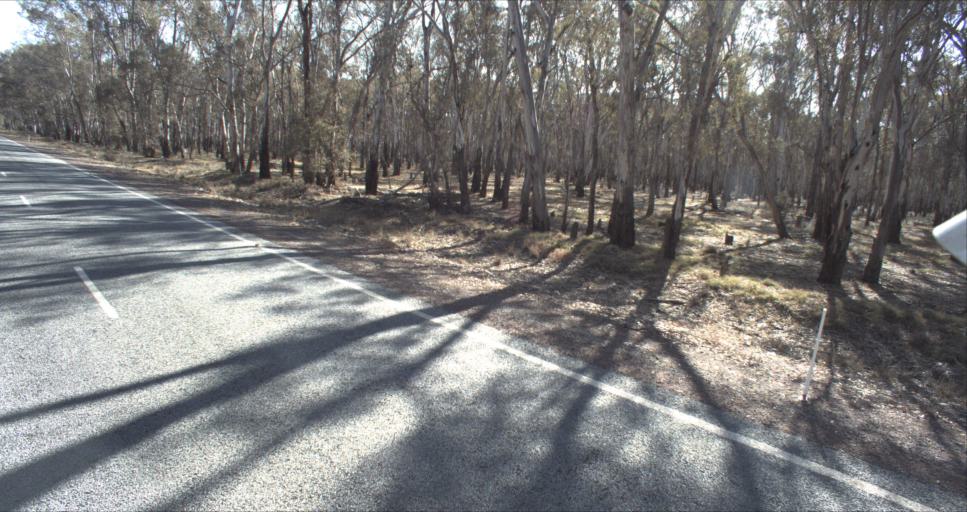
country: AU
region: New South Wales
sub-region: Leeton
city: Leeton
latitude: -34.6271
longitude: 146.3786
